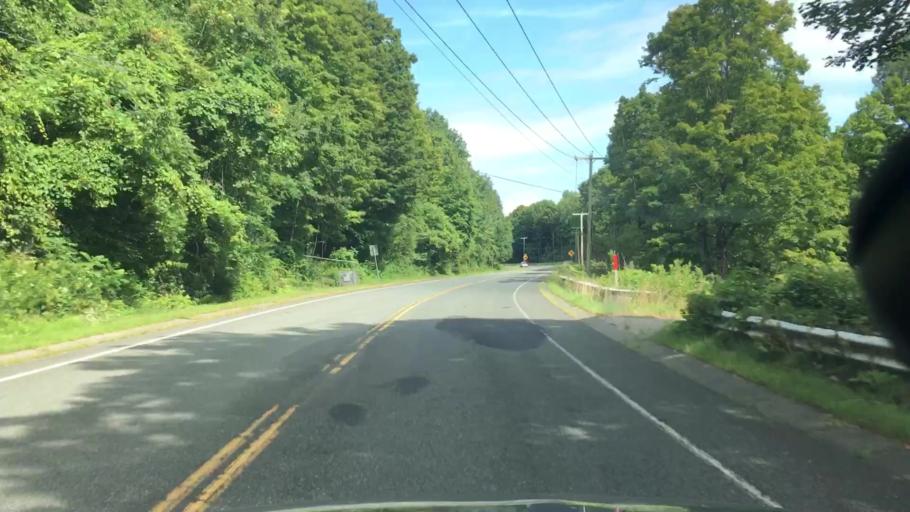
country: US
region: Massachusetts
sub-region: Franklin County
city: Colrain
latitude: 42.6616
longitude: -72.6817
